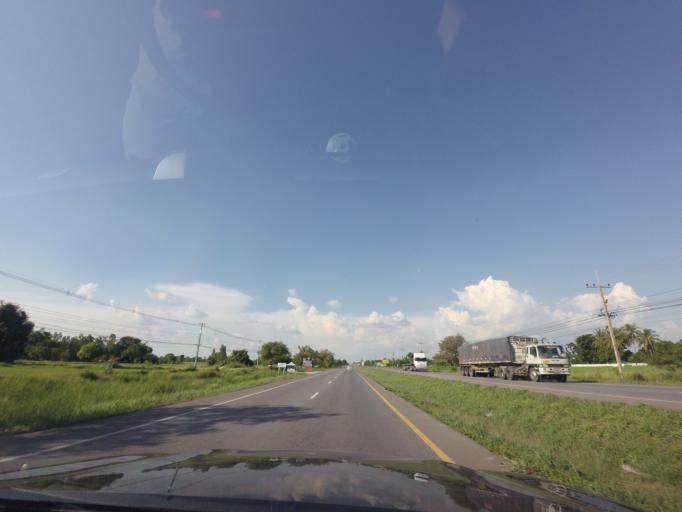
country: TH
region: Khon Kaen
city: Non Sila
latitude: 15.9864
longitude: 102.6975
